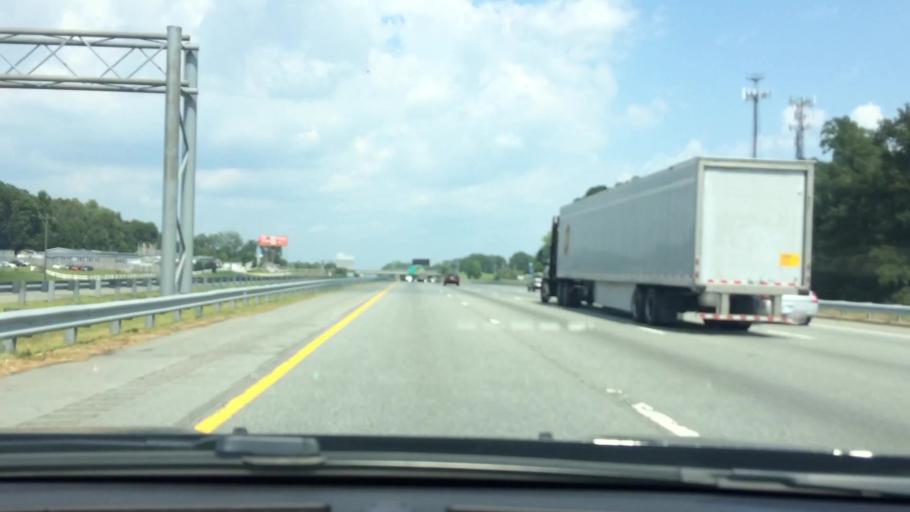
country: US
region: North Carolina
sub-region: Guilford County
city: Greensboro
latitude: 36.0079
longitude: -79.8461
